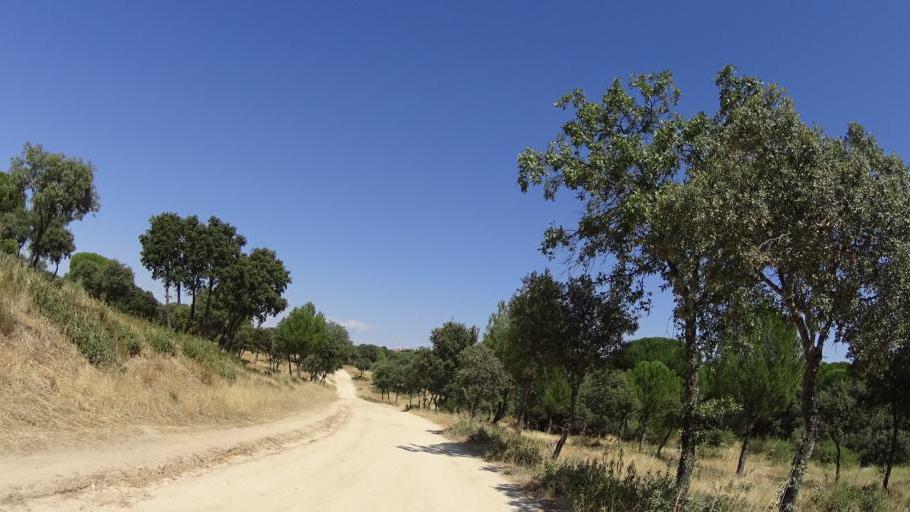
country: ES
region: Madrid
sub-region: Provincia de Madrid
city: Boadilla del Monte
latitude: 40.4323
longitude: -3.8551
